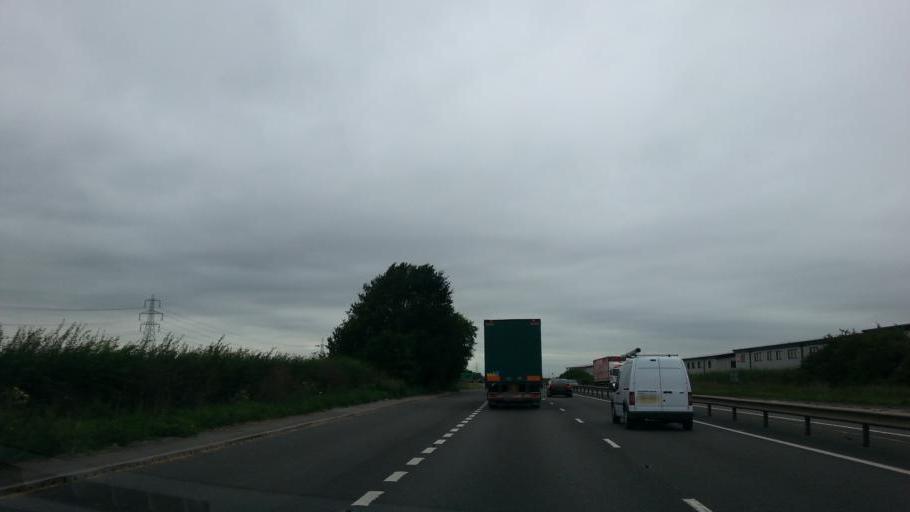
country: GB
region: England
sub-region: Lincolnshire
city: Long Bennington
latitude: 53.0019
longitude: -0.7626
